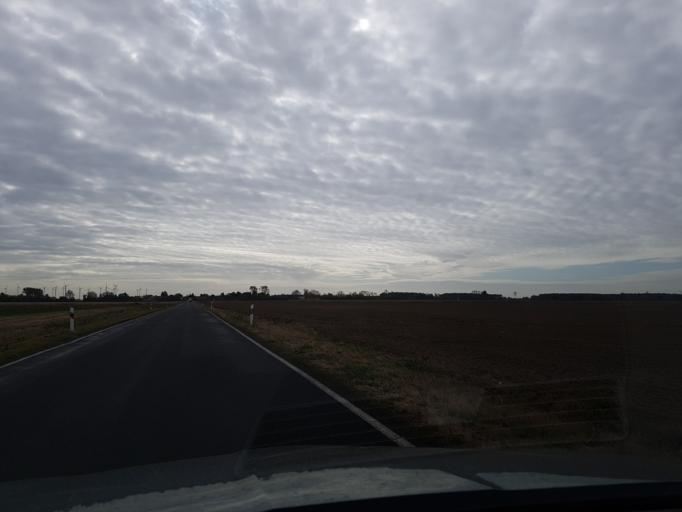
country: DE
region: Brandenburg
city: Falkenberg
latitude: 51.5500
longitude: 13.2716
